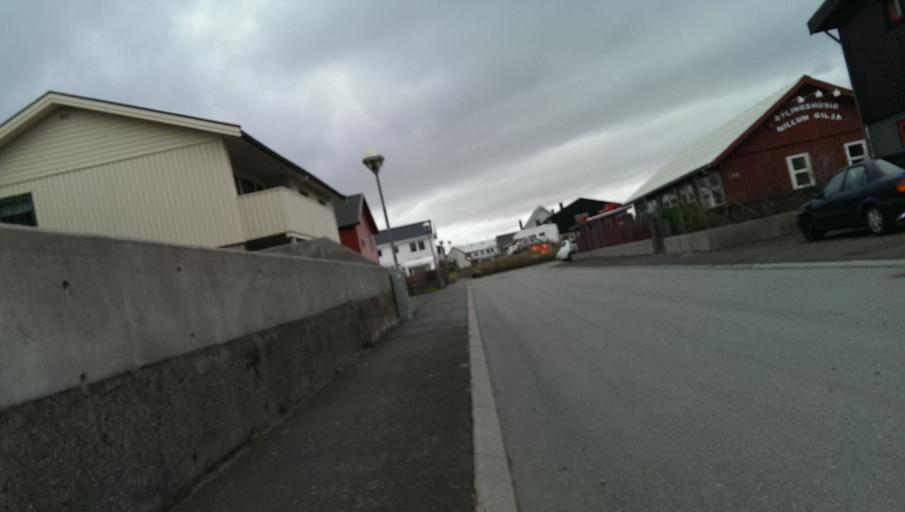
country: FO
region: Streymoy
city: Hoyvik
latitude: 62.0341
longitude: -6.7916
